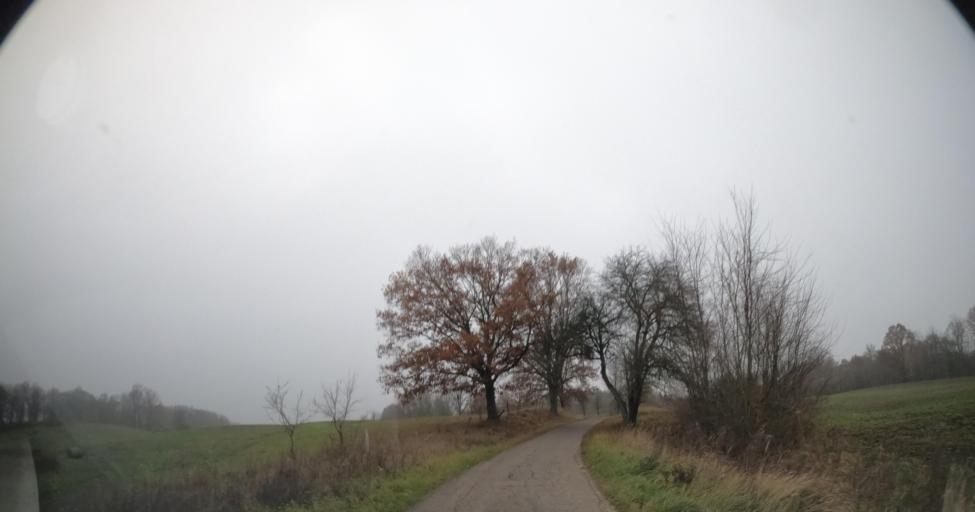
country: PL
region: West Pomeranian Voivodeship
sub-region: Powiat drawski
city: Drawsko Pomorskie
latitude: 53.5785
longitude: 15.8108
